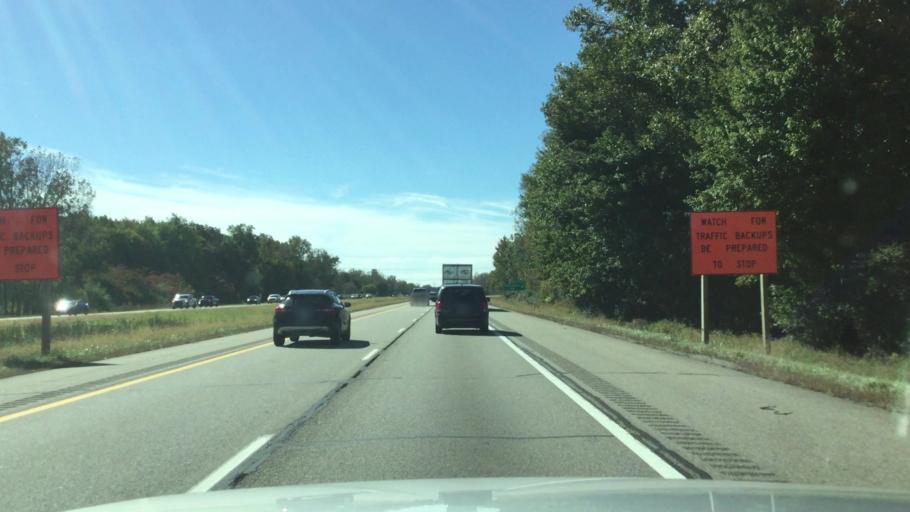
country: US
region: Michigan
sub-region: Wayne County
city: Plymouth
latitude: 42.3652
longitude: -83.5567
